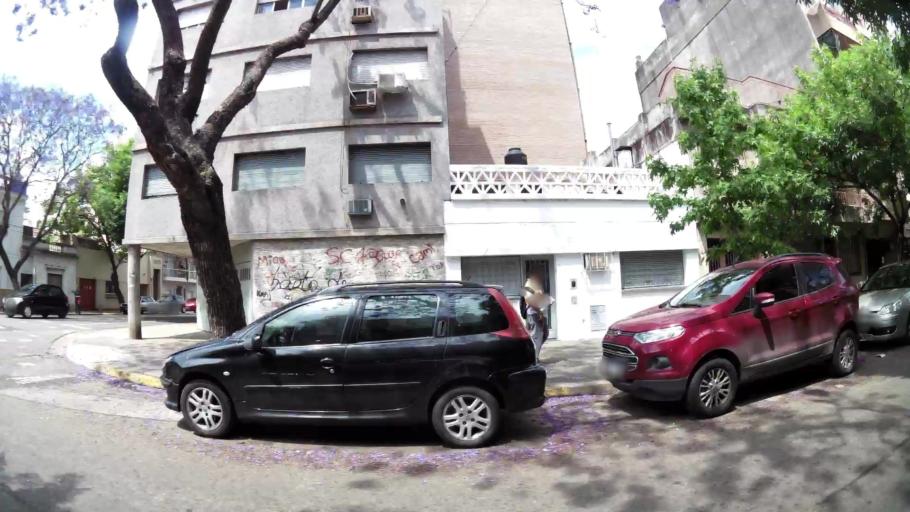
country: AR
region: Santa Fe
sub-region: Departamento de Rosario
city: Rosario
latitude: -32.9606
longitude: -60.6361
